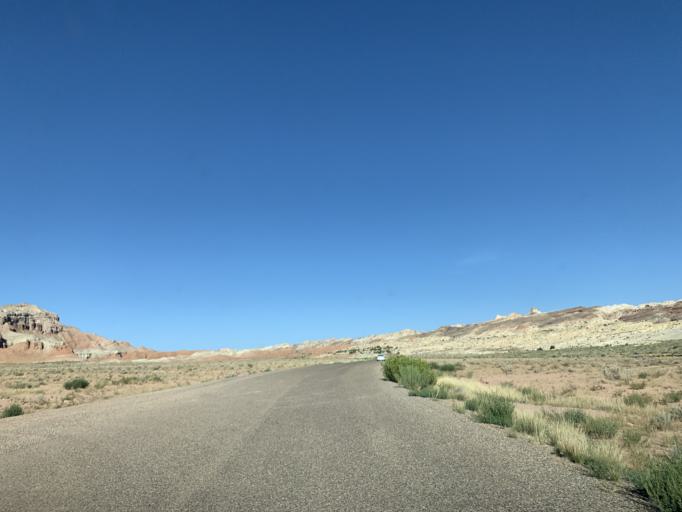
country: US
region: Utah
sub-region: Emery County
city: Ferron
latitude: 38.5791
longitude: -110.7672
